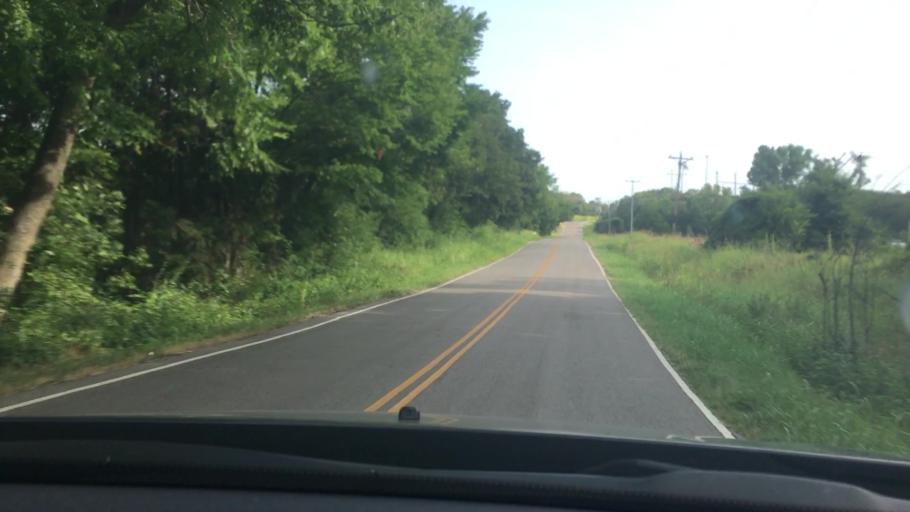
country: US
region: Oklahoma
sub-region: Pontotoc County
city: Byng
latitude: 34.8611
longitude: -96.6135
